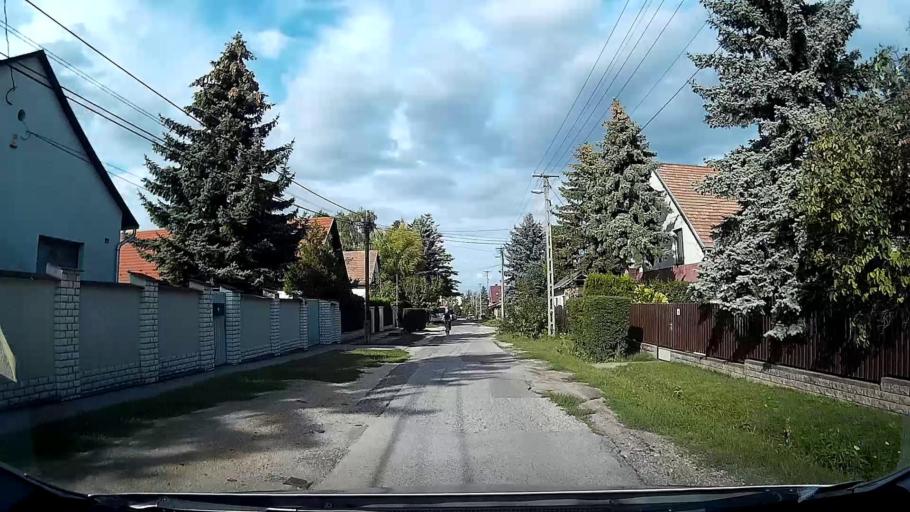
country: HU
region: Pest
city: Pomaz
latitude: 47.6386
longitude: 19.0311
